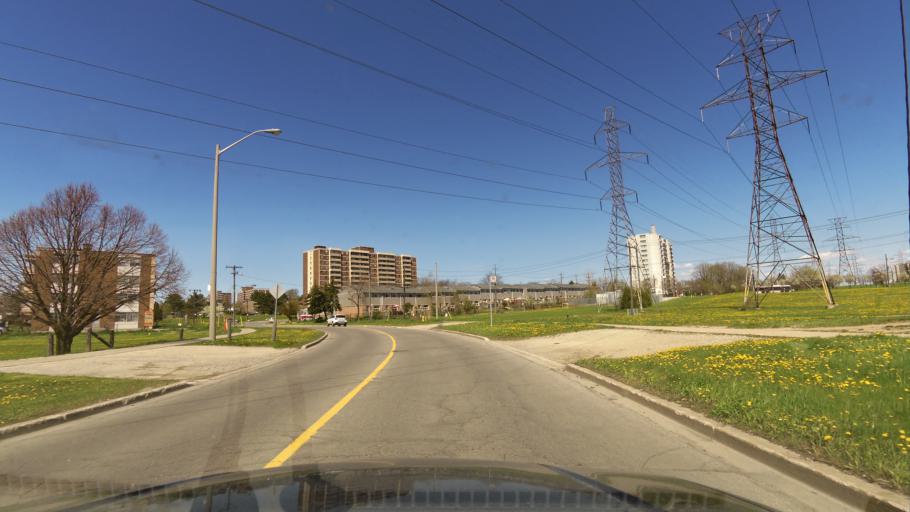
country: CA
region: Ontario
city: Concord
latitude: 43.7598
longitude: -79.5209
